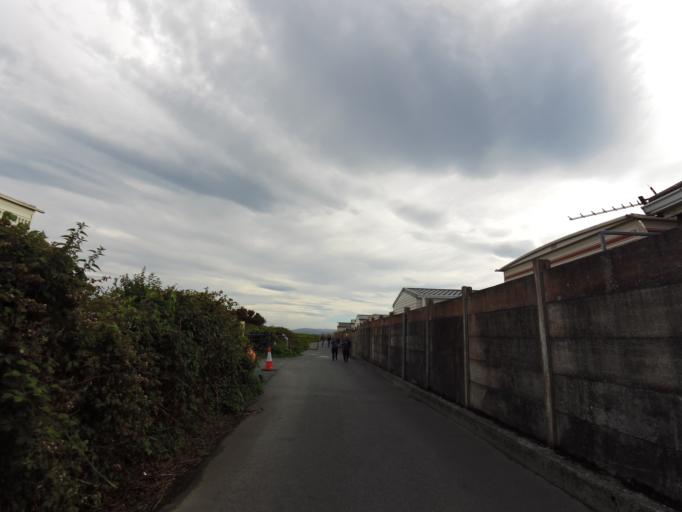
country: IE
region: Connaught
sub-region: County Galway
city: Bearna
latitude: 53.2566
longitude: -9.1047
